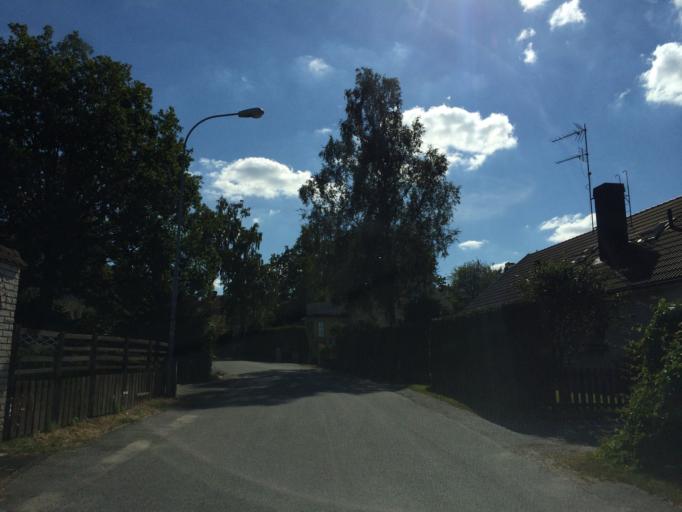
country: SE
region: Stockholm
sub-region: Sollentuna Kommun
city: Sollentuna
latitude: 59.4560
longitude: 17.9113
